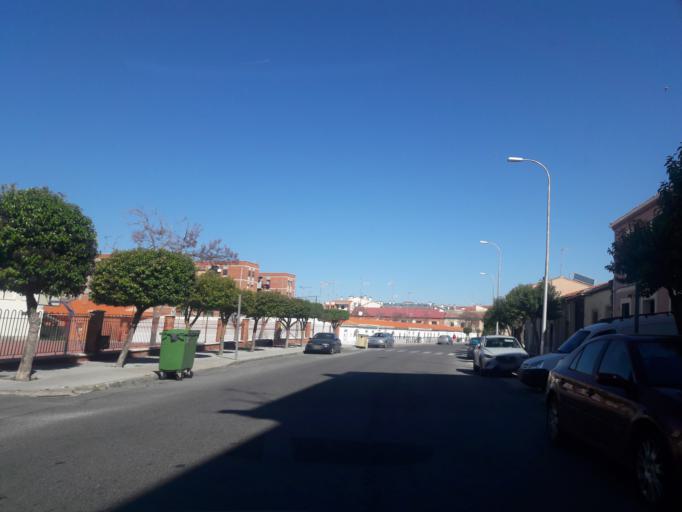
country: ES
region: Castille and Leon
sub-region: Provincia de Salamanca
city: Penaranda de Bracamonte
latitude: 40.8970
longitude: -5.2007
